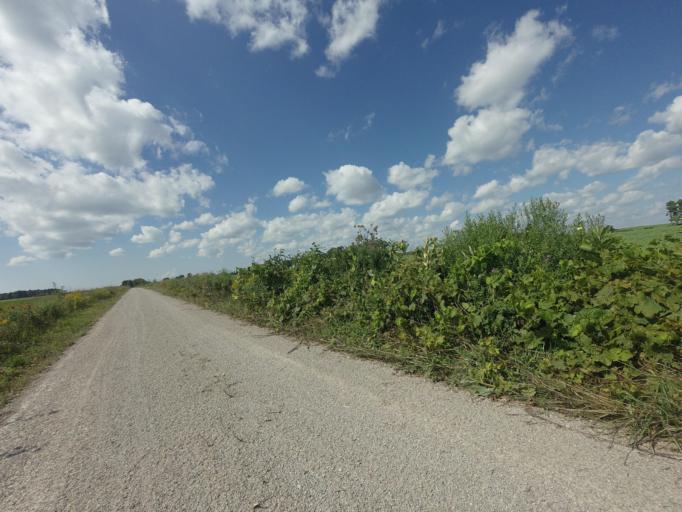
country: CA
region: Ontario
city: Huron East
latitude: 43.7132
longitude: -81.3796
